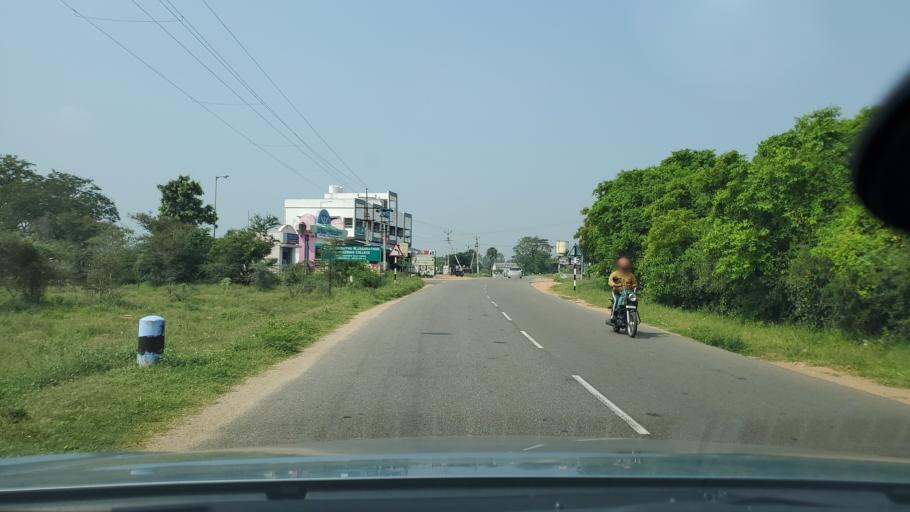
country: IN
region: Tamil Nadu
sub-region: Erode
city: Chennimalai
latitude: 11.1921
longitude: 77.6233
